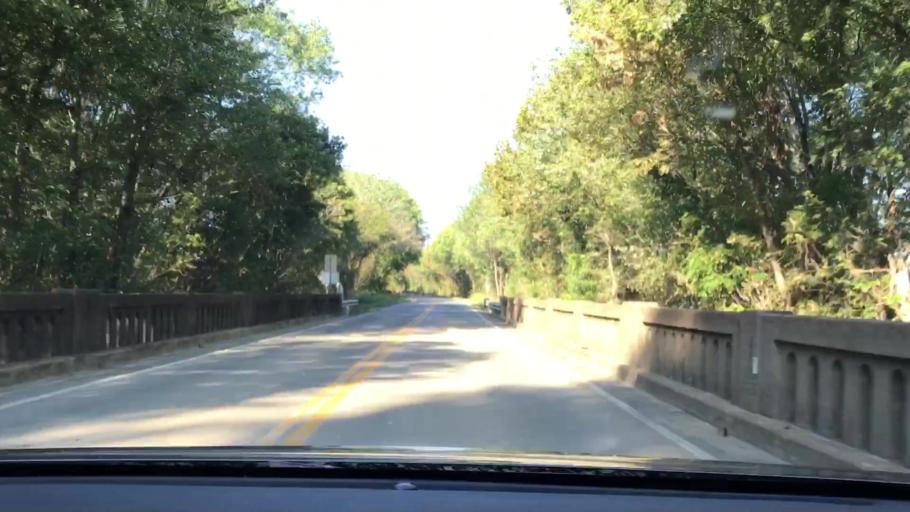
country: US
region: Kentucky
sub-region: Marshall County
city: Benton
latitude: 36.7687
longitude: -88.2789
